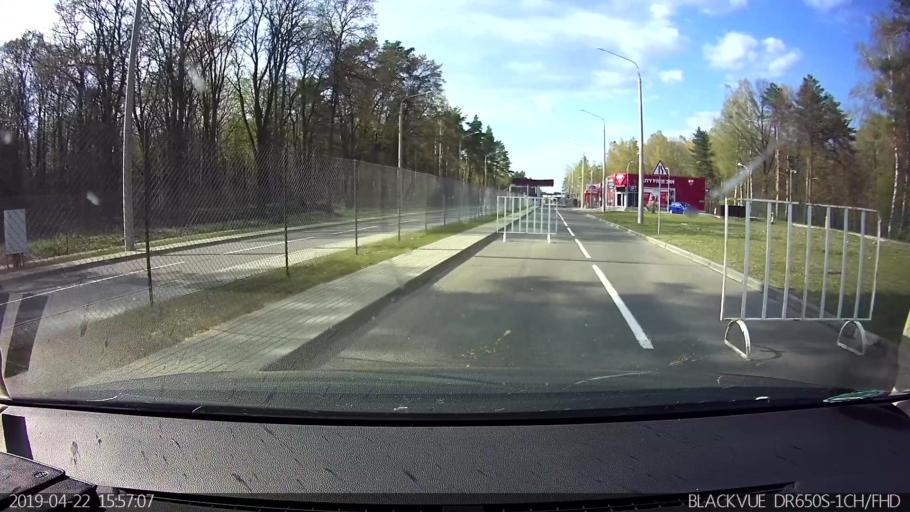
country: PL
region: Podlasie
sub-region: Powiat hajnowski
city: Czeremcha
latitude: 52.4681
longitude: 23.3593
